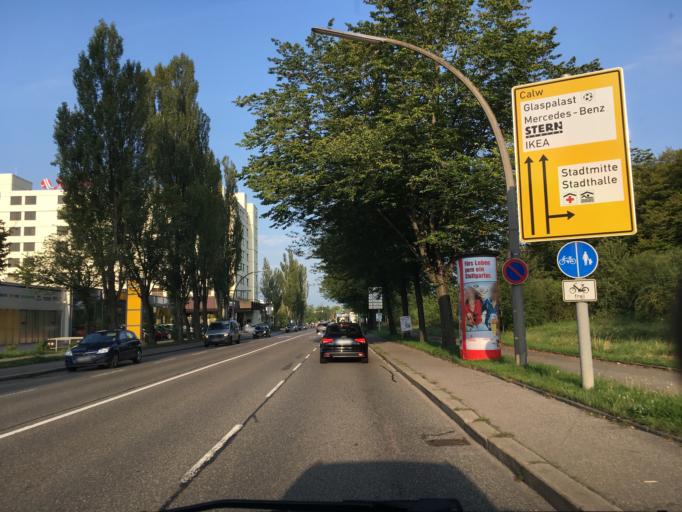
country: DE
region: Baden-Wuerttemberg
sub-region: Regierungsbezirk Stuttgart
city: Sindelfingen
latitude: 48.7071
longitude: 9.0233
